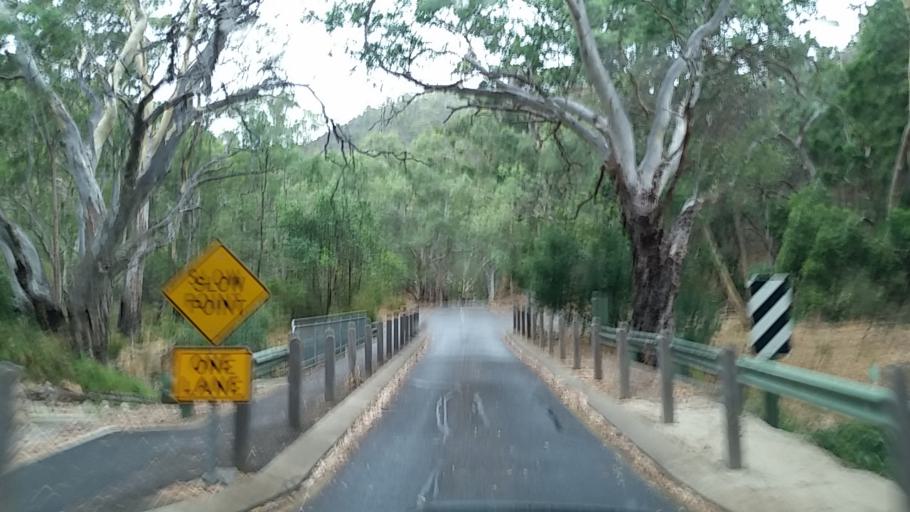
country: AU
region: South Australia
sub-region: Adelaide Hills
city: Adelaide Hills
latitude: -34.9010
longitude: 138.7005
